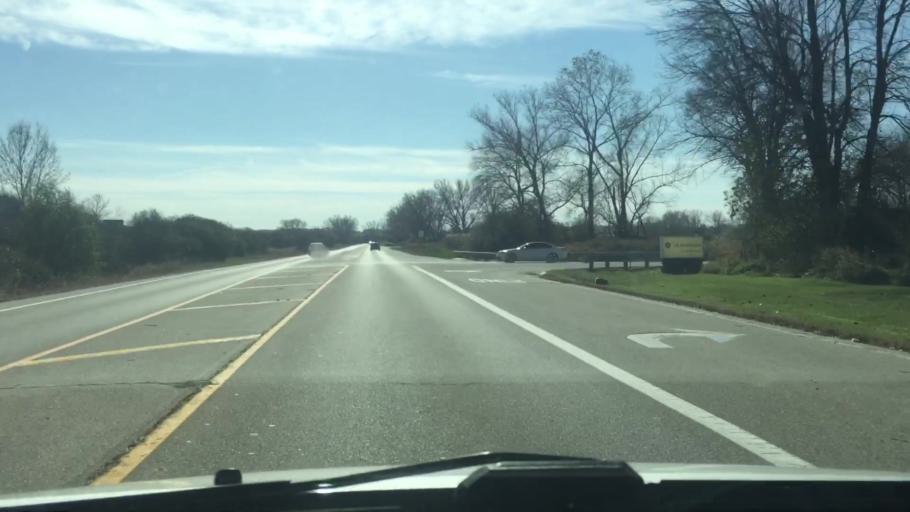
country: US
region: Wisconsin
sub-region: Waukesha County
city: Pewaukee
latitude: 43.0600
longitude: -88.2522
